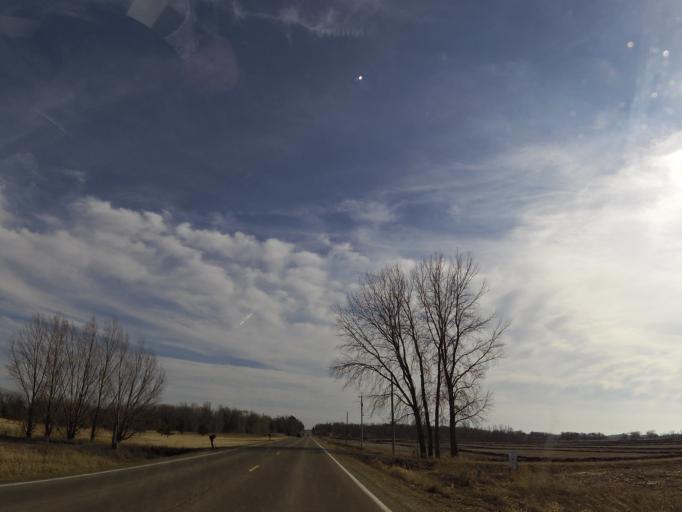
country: US
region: Minnesota
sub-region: Rice County
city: Northfield
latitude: 44.4977
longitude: -93.2000
